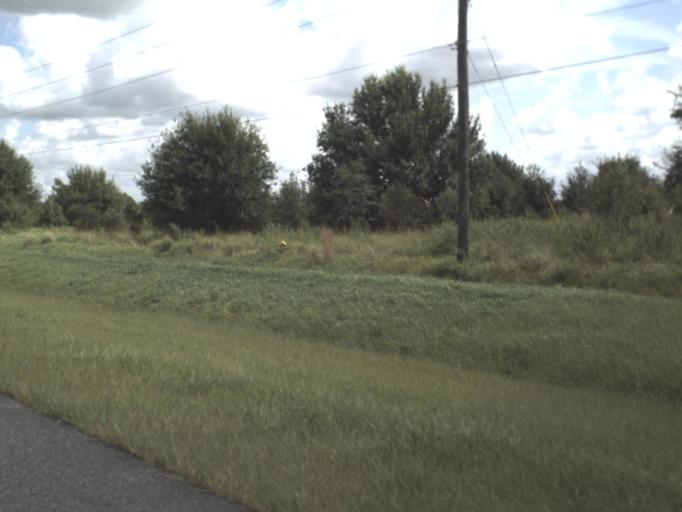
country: US
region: Florida
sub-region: Charlotte County
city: Harbour Heights
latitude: 27.0739
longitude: -81.9581
